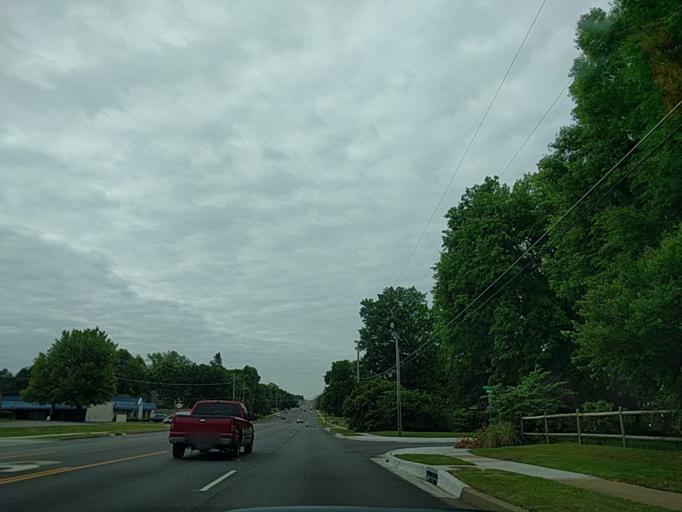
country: US
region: Oklahoma
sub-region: Tulsa County
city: Jenks
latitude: 36.0871
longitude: -95.9045
